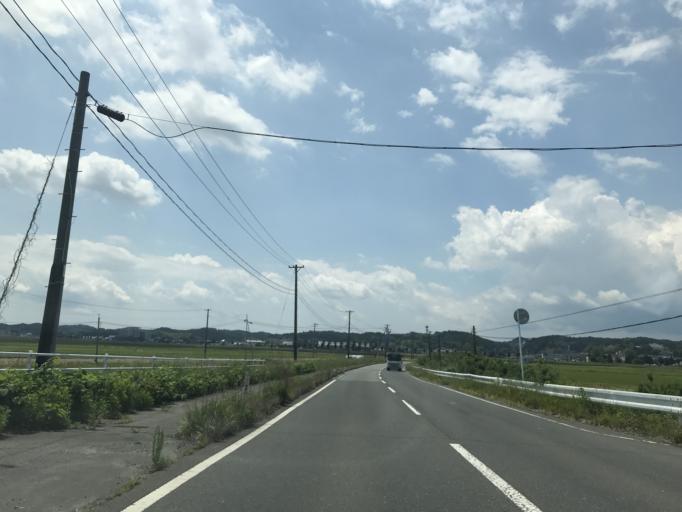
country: JP
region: Miyagi
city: Kogota
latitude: 38.5244
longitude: 141.0579
